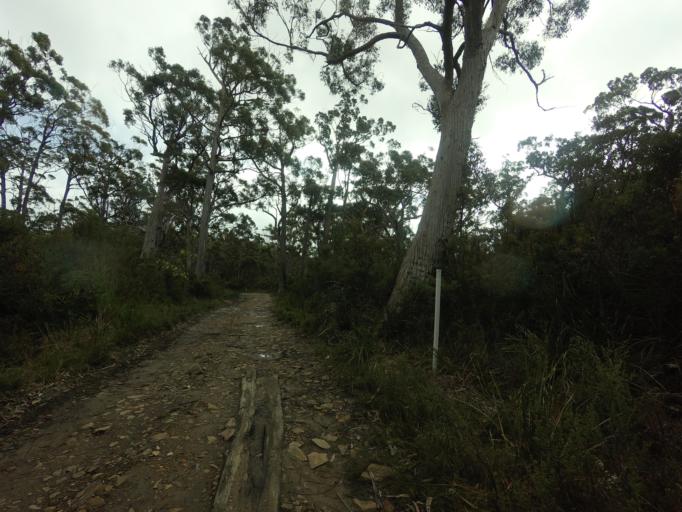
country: AU
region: Tasmania
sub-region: Huon Valley
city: Geeveston
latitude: -43.4735
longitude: 146.9344
